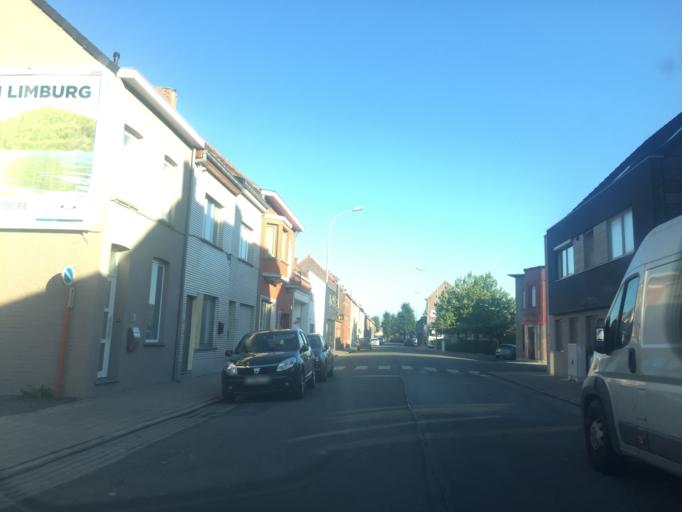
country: BE
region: Flanders
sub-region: Provincie West-Vlaanderen
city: Izegem
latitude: 50.9104
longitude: 3.2178
